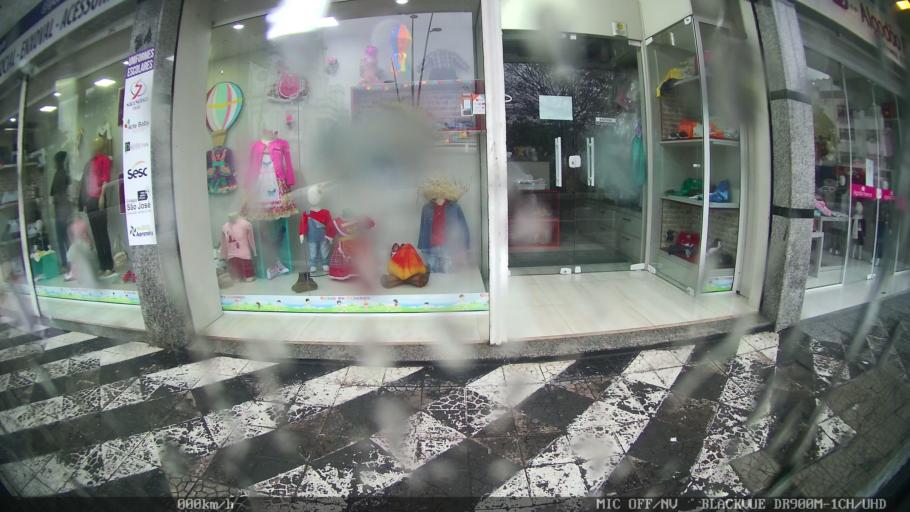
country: BR
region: Santa Catarina
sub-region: Itajai
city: Itajai
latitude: -26.9069
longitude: -48.6621
